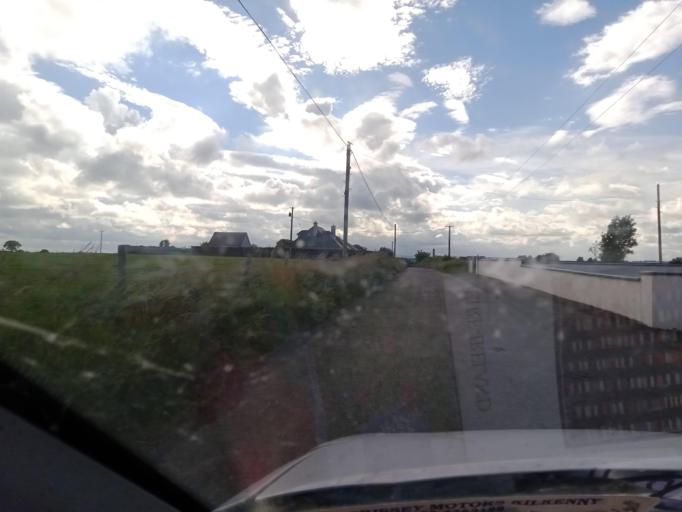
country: IE
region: Leinster
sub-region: Laois
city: Rathdowney
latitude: 52.7761
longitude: -7.5303
